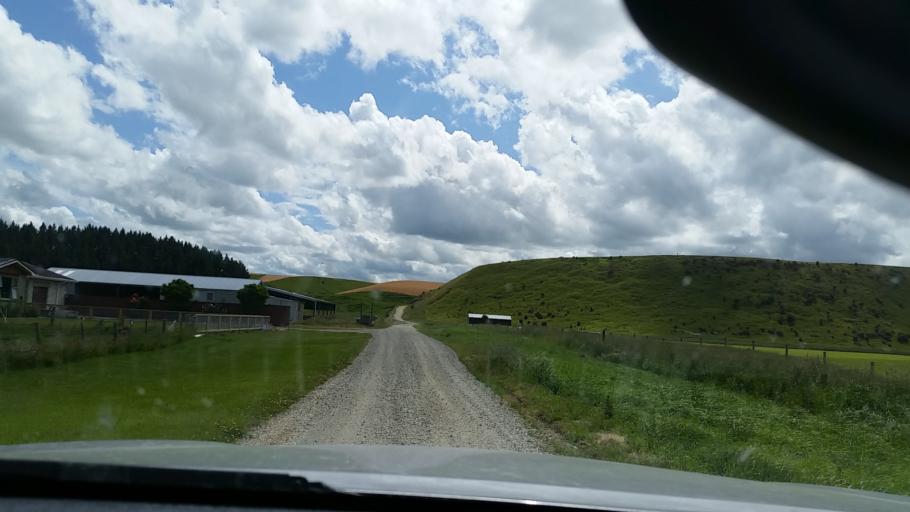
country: NZ
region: Southland
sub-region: Gore District
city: Gore
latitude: -45.7844
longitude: 168.7829
